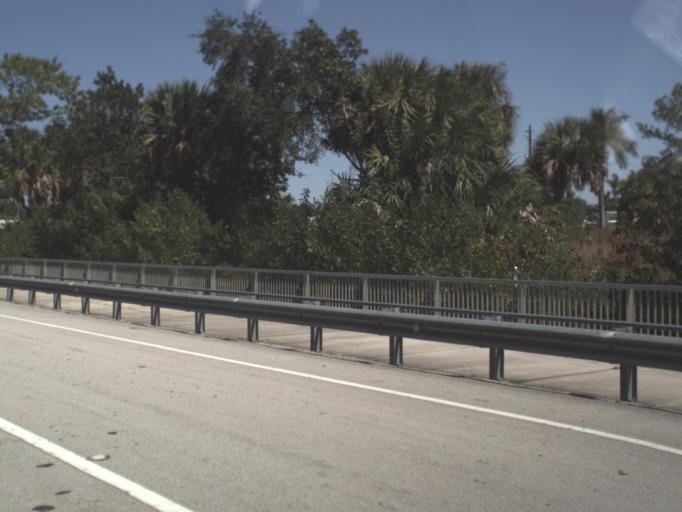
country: US
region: Florida
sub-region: Collier County
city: Lely Resort
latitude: 26.0532
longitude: -81.6996
